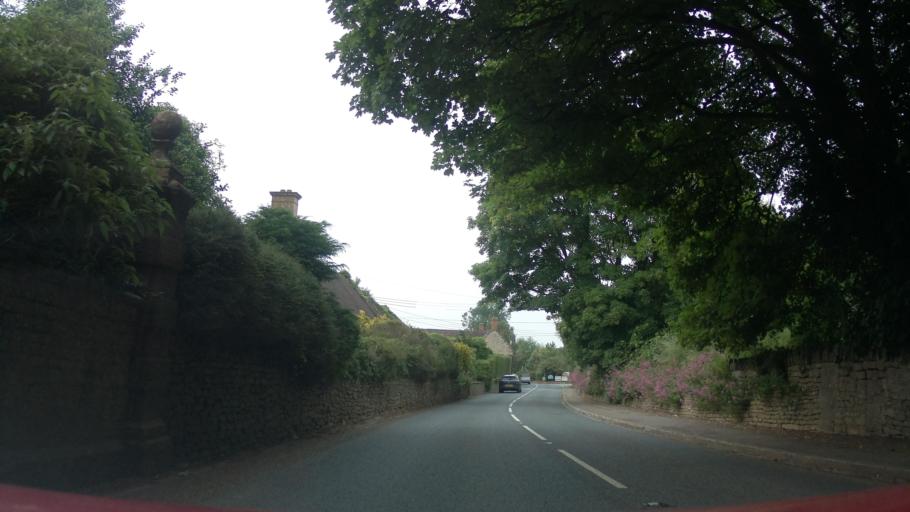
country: GB
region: England
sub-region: Somerset
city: Crewkerne
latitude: 50.8848
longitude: -2.7480
